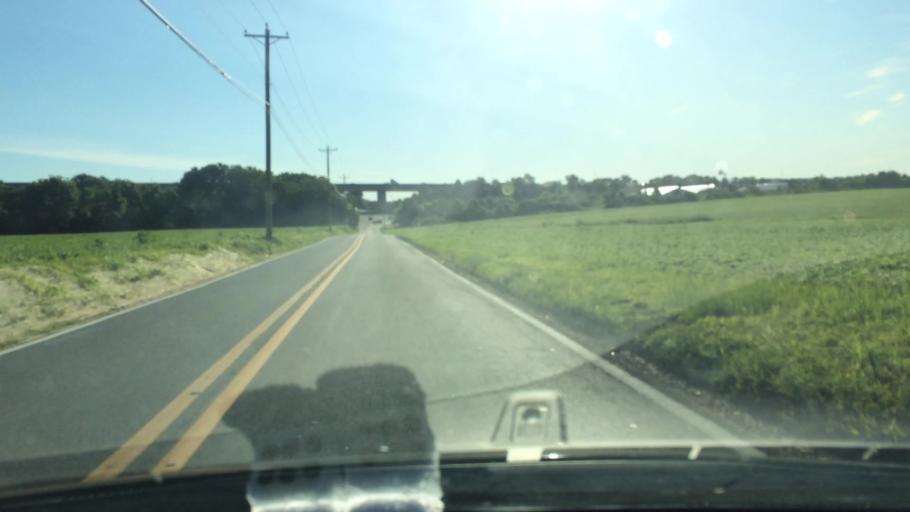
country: US
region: Delaware
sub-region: New Castle County
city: Delaware City
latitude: 39.5431
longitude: -75.6580
